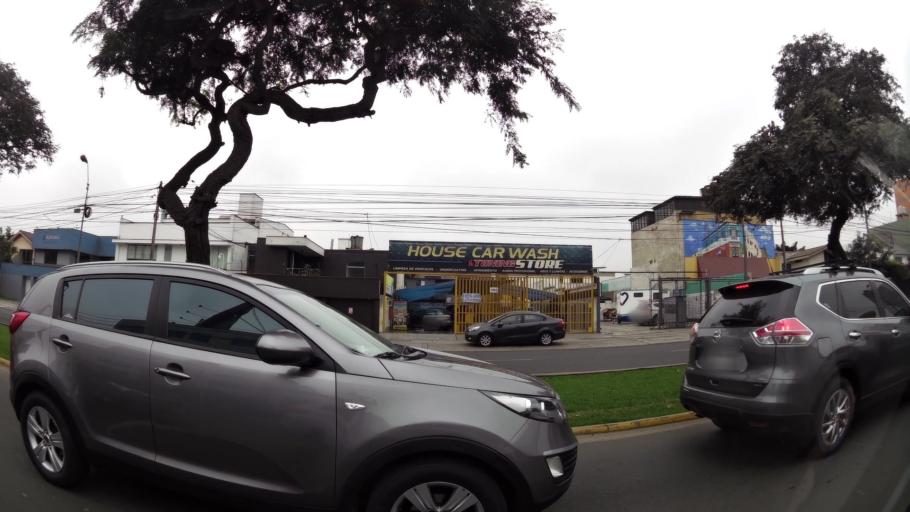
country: PE
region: Lima
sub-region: Lima
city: Surco
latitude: -12.1275
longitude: -77.0109
